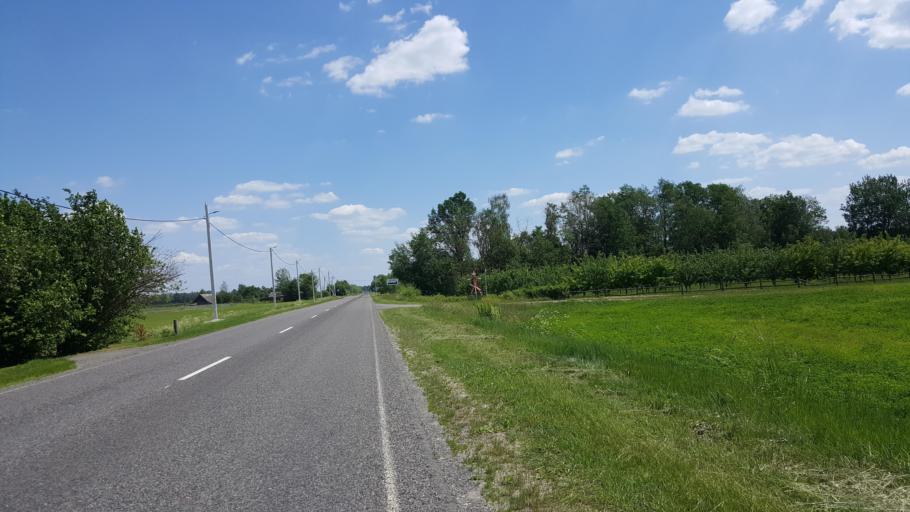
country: BY
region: Brest
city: Kobryn
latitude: 52.2011
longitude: 24.1974
